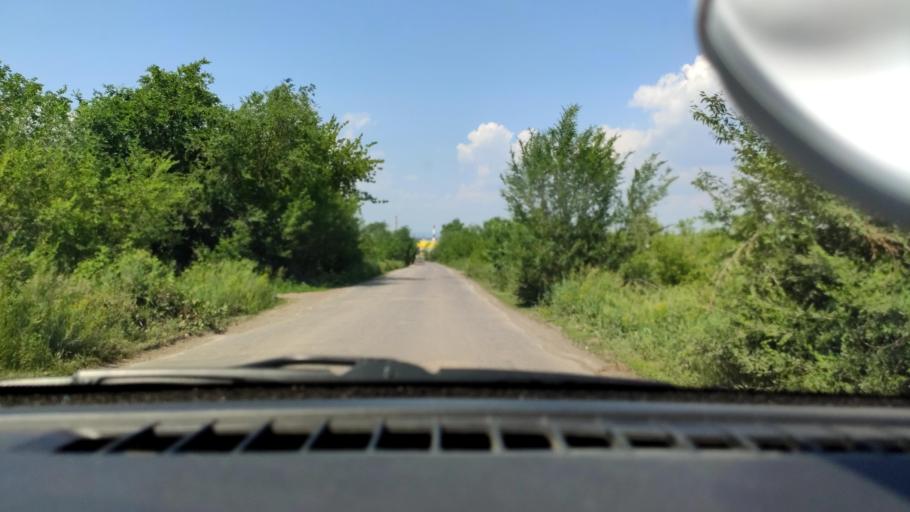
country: RU
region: Samara
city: Novokuybyshevsk
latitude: 53.0789
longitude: 50.0666
